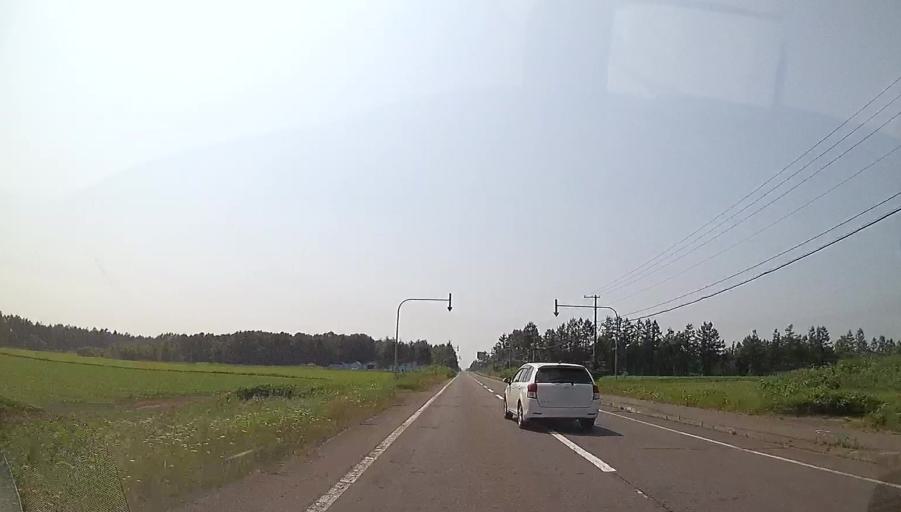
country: JP
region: Hokkaido
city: Otofuke
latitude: 43.1707
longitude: 143.1089
